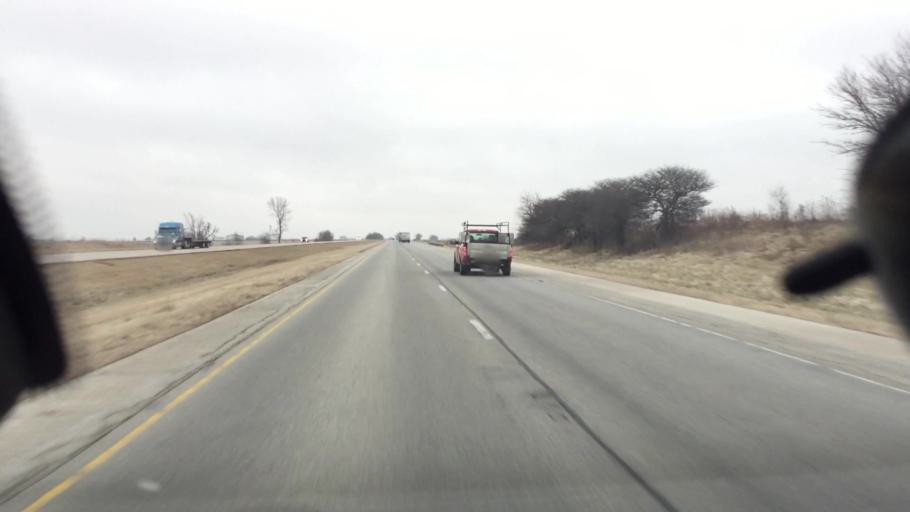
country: US
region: Illinois
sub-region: Knox County
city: Galesburg
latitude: 41.1056
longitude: -90.3332
